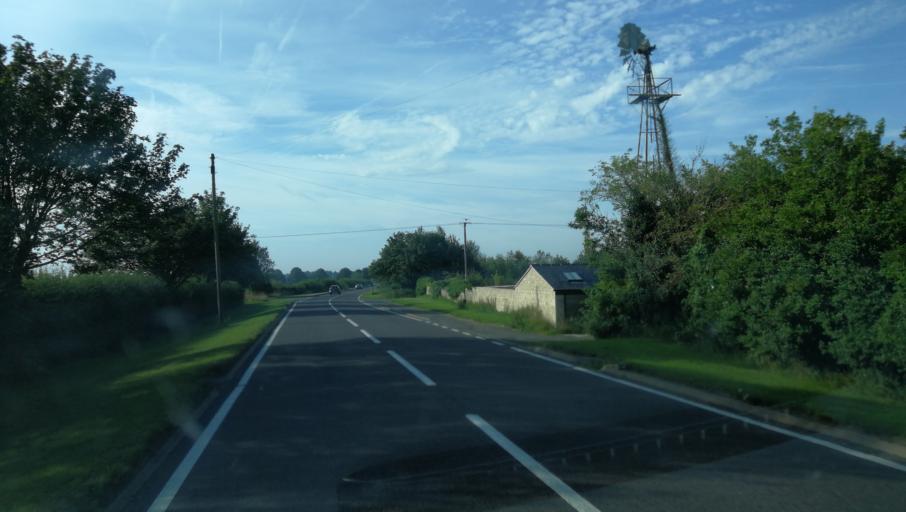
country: GB
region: England
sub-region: Oxfordshire
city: Deddington
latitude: 51.9340
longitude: -1.3261
